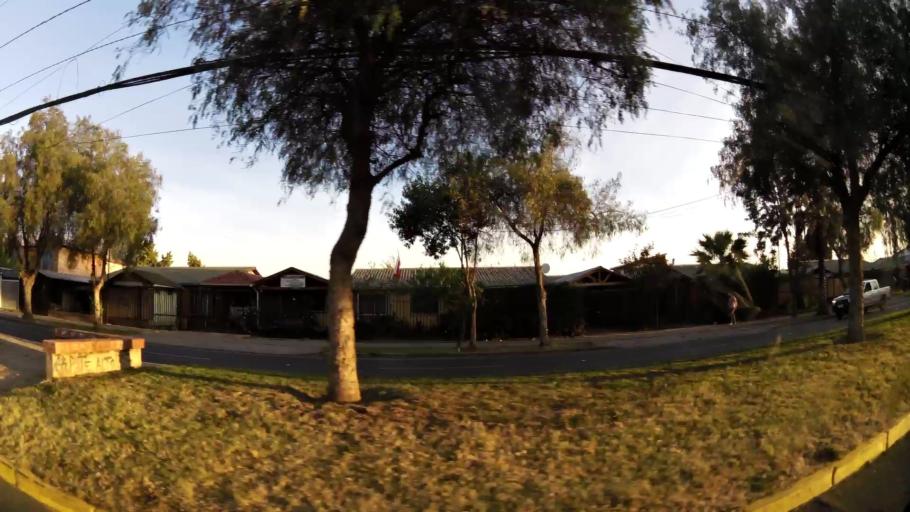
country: CL
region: Santiago Metropolitan
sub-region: Provincia de Cordillera
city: Puente Alto
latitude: -33.5976
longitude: -70.5733
